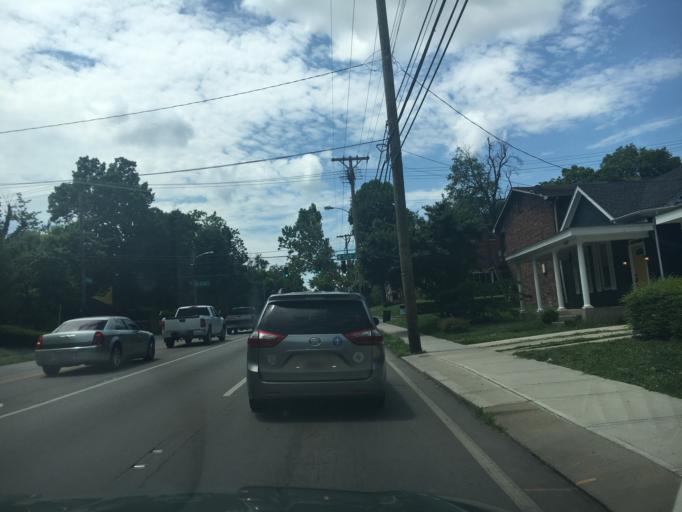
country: US
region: Kentucky
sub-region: Fayette County
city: Lexington-Fayette
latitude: 38.0569
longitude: -84.4886
